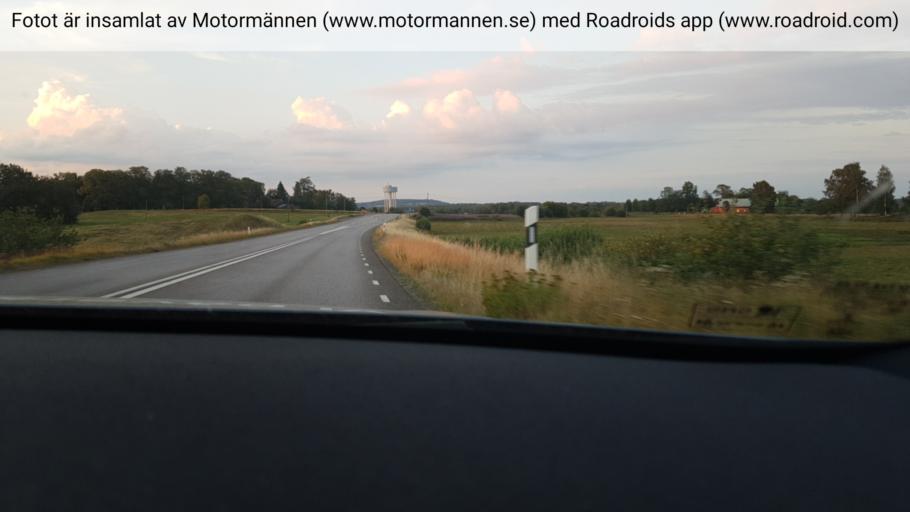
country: SE
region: Vaestra Goetaland
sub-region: Falkopings Kommun
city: Akarp
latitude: 58.2595
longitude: 13.7041
